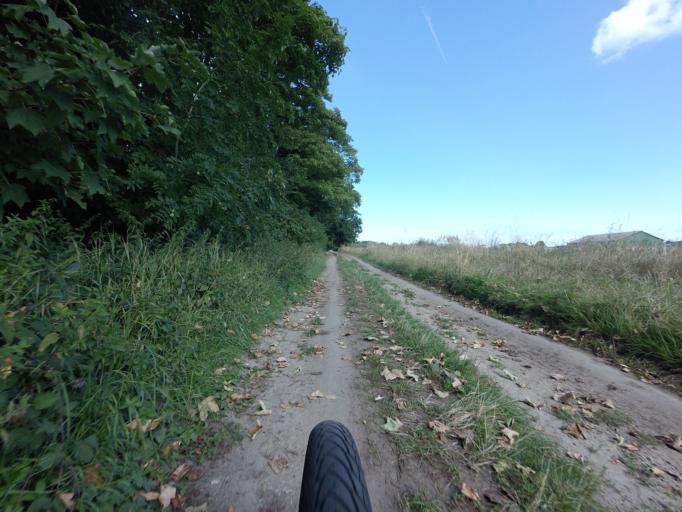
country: DK
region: Zealand
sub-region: Vordingborg Kommune
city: Stege
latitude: 54.9677
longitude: 12.4151
